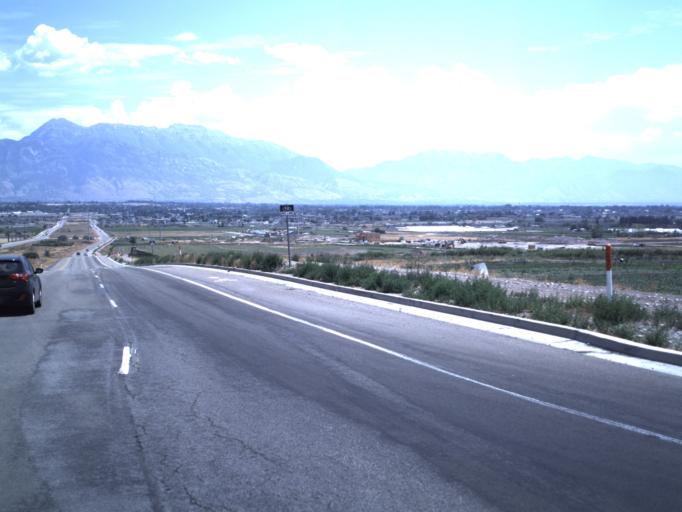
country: US
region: Utah
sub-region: Utah County
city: Saratoga Springs
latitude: 40.4126
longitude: -111.9226
